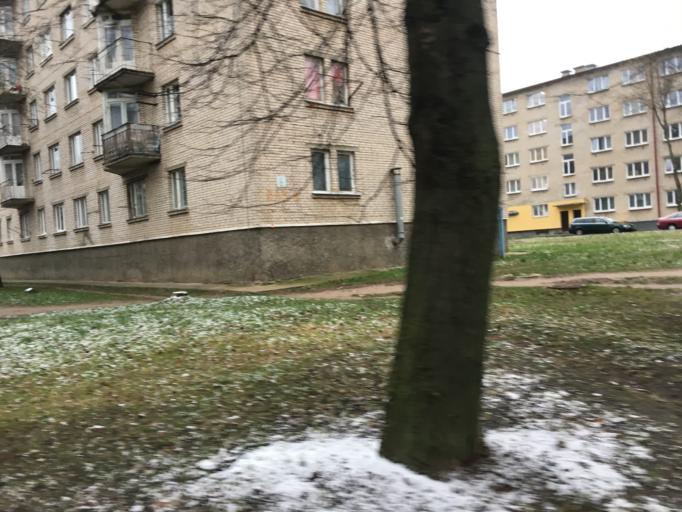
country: BY
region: Grodnenskaya
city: Hrodna
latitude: 53.6998
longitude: 23.8149
